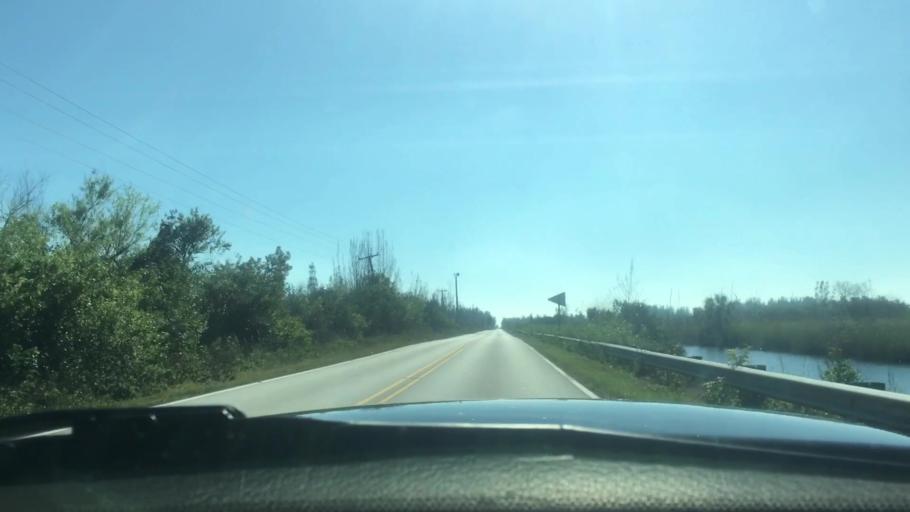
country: US
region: Florida
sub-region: Miami-Dade County
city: Florida City
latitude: 25.4284
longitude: -80.4699
